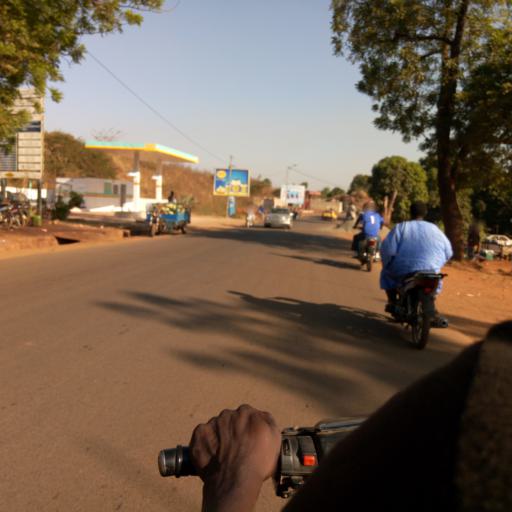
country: ML
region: Bamako
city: Bamako
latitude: 12.6598
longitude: -8.0333
